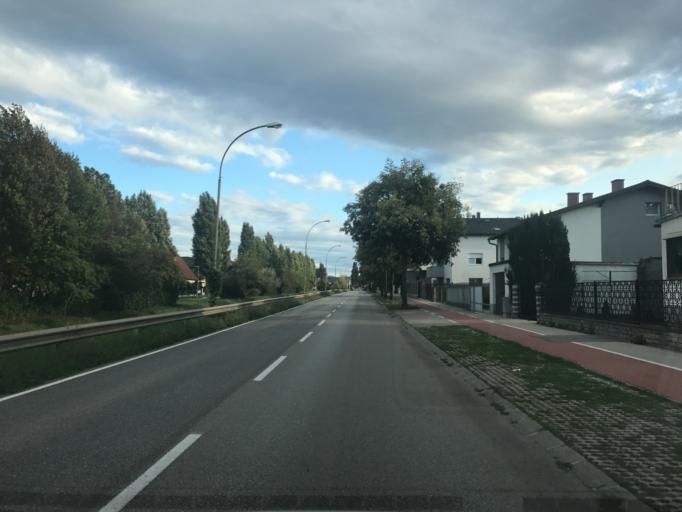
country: AT
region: Lower Austria
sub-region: Wiener Neustadt Stadt
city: Wiener Neustadt
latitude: 47.8213
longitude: 16.2580
